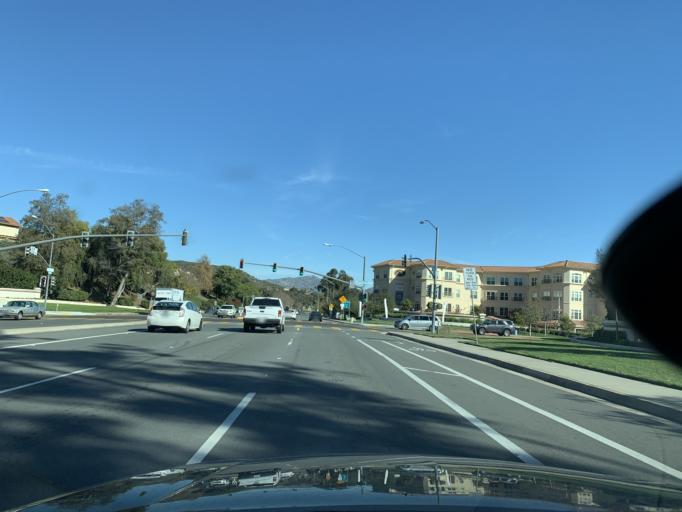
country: US
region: California
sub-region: San Diego County
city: Poway
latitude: 32.9466
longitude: -117.0787
